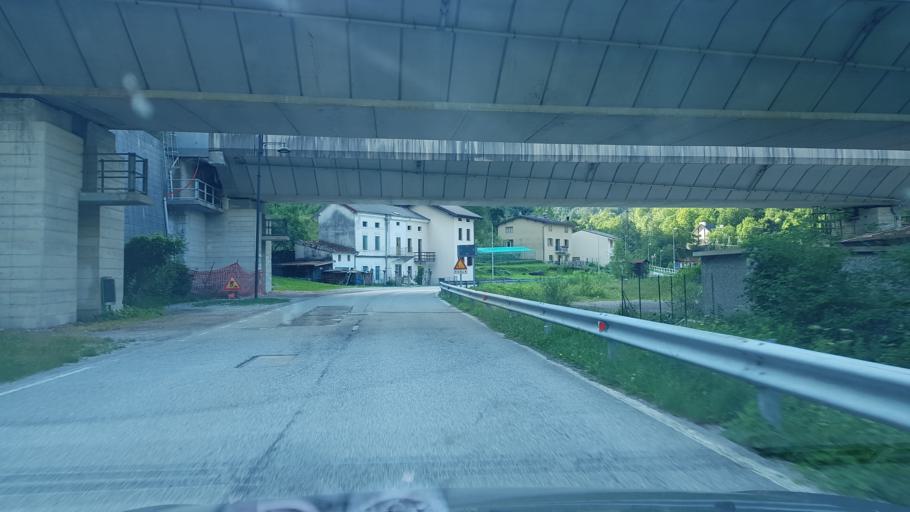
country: IT
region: Friuli Venezia Giulia
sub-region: Provincia di Udine
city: Chiusaforte
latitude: 46.4073
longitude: 13.3155
